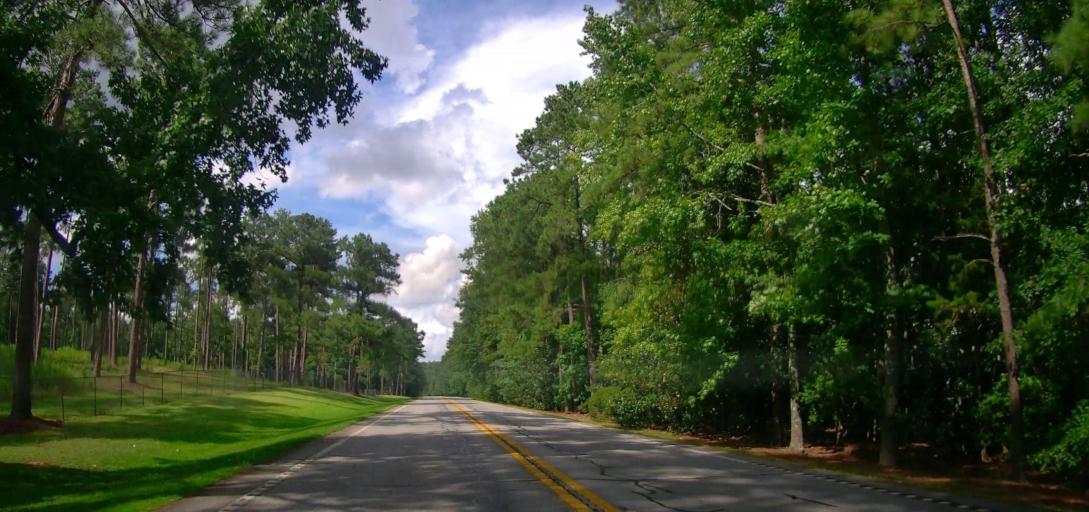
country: US
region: Georgia
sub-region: Harris County
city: Pine Mountain
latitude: 32.8402
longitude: -84.8435
